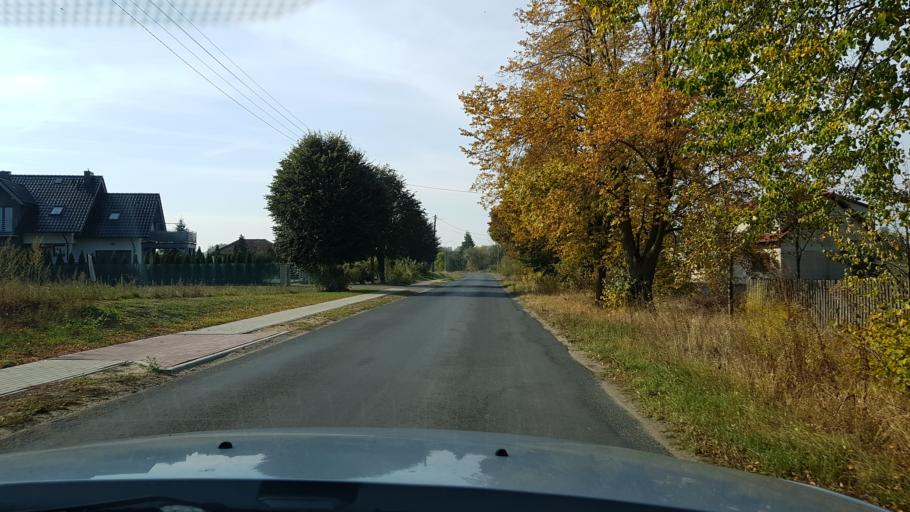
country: PL
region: West Pomeranian Voivodeship
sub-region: Powiat mysliborski
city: Barlinek
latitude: 52.9821
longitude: 15.1807
